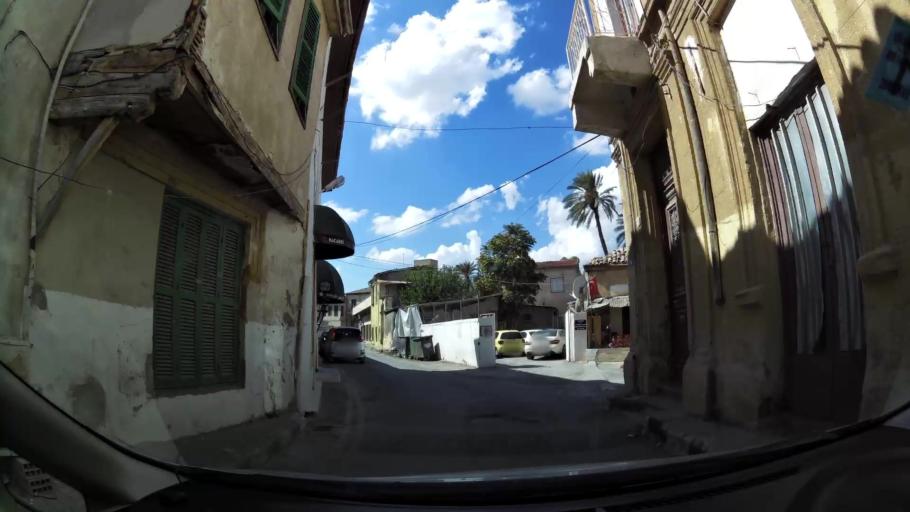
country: CY
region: Lefkosia
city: Nicosia
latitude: 35.1787
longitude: 33.3582
